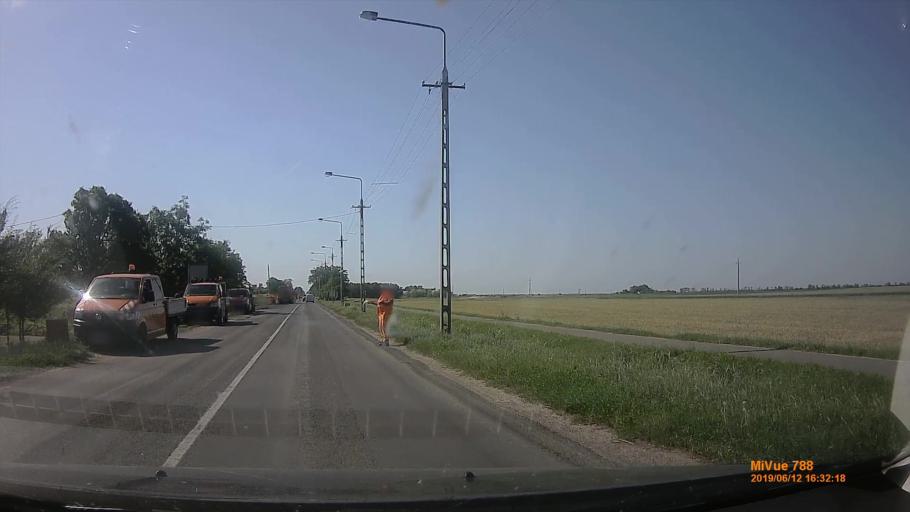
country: HU
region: Csongrad
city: Apatfalva
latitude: 46.1815
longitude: 20.5704
